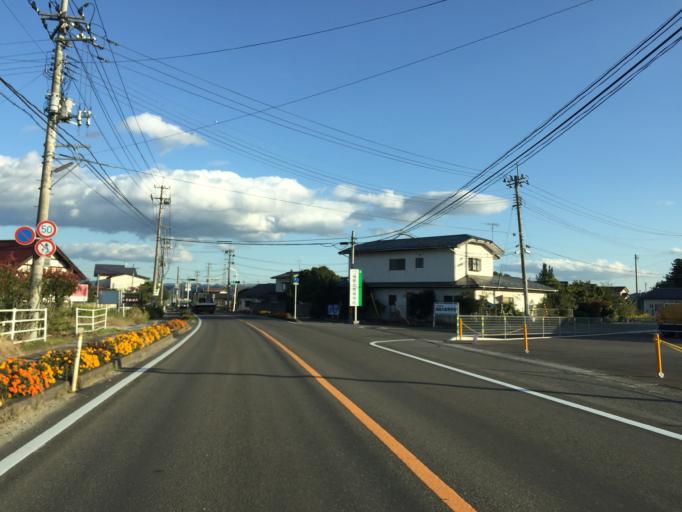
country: JP
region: Fukushima
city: Fukushima-shi
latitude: 37.8192
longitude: 140.4520
